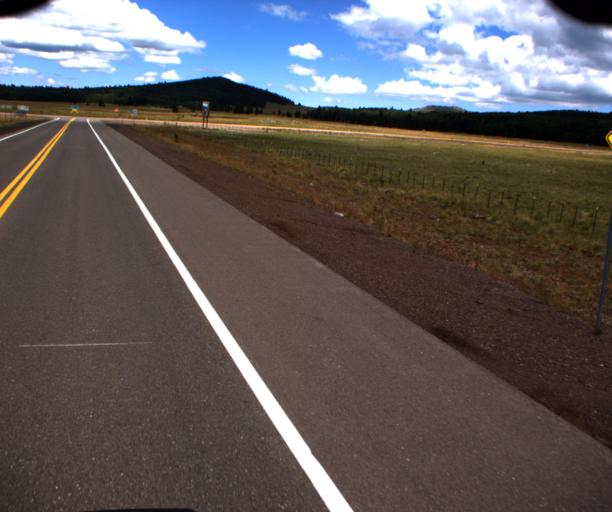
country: US
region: Arizona
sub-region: Apache County
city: Eagar
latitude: 34.0417
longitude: -109.5911
